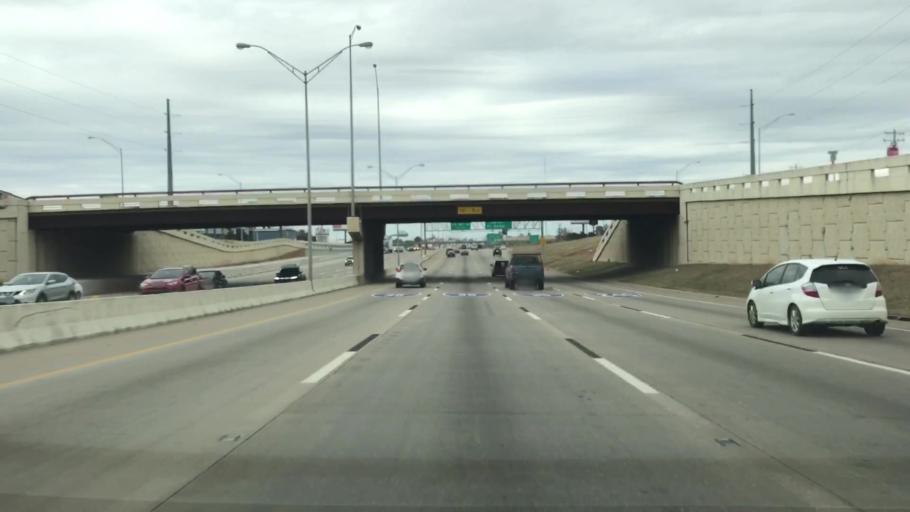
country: US
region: Oklahoma
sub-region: Cleveland County
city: Moore
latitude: 35.3839
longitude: -97.4940
